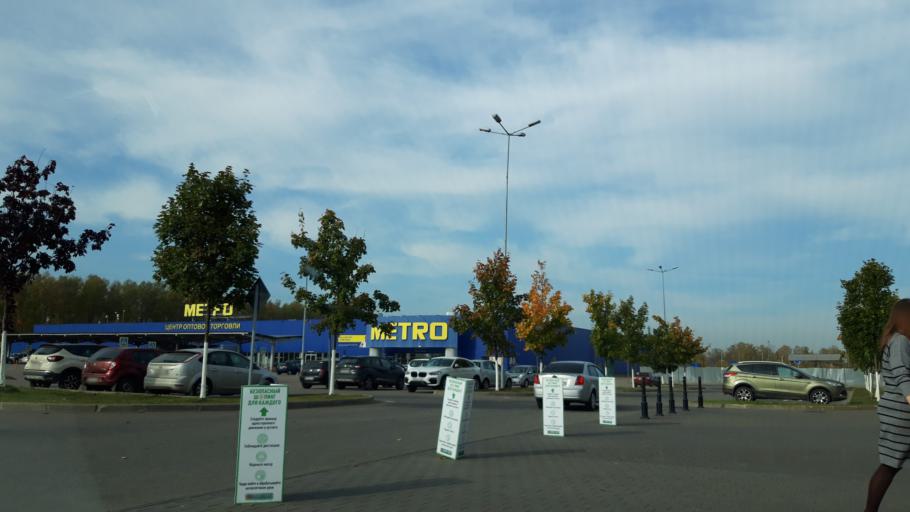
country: RU
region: Moskovskaya
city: Skhodnya
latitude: 55.9808
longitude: 37.3015
